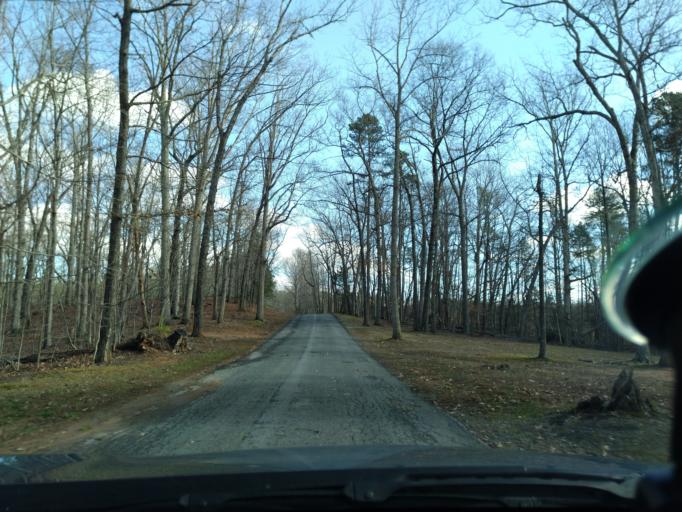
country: US
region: Virginia
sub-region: Nottoway County
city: Crewe
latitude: 37.1737
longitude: -78.2688
